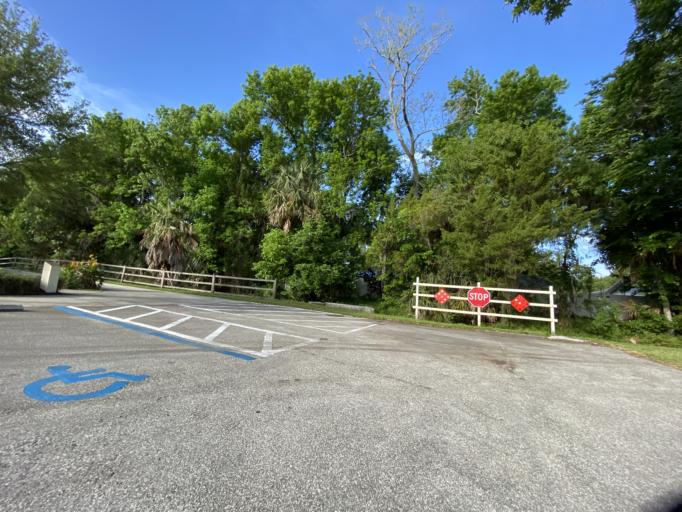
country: US
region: Florida
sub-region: Volusia County
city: South Daytona
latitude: 29.1726
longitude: -81.0139
